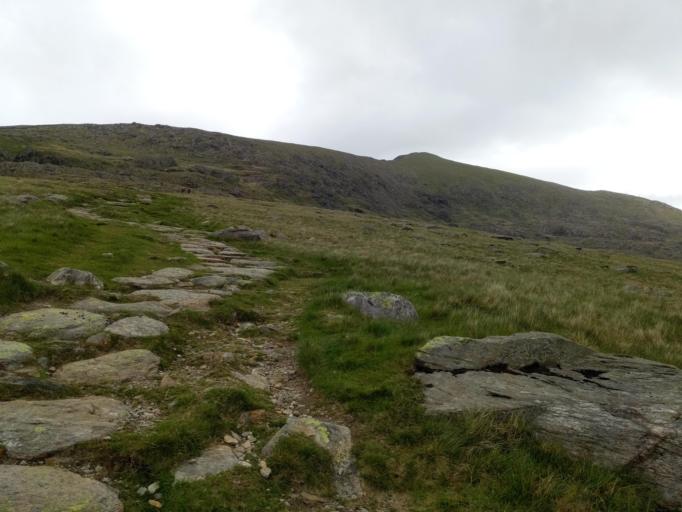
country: GB
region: Wales
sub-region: Gwynedd
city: Llanberis
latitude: 53.0559
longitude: -4.1049
